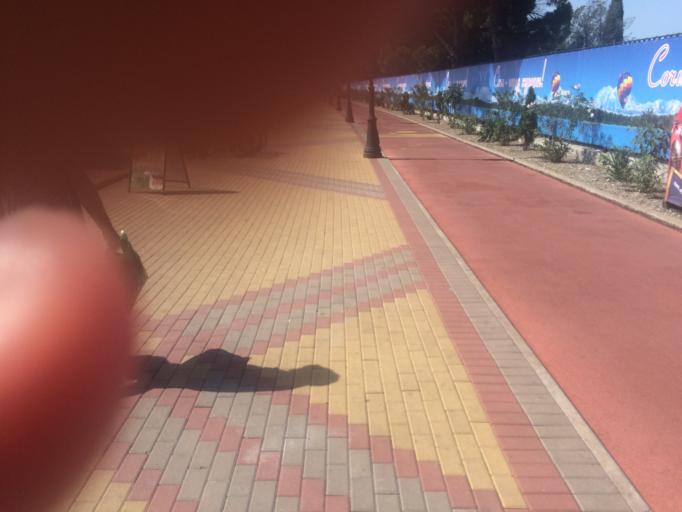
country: RU
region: Krasnodarskiy
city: Adler
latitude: 43.3974
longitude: 39.9673
